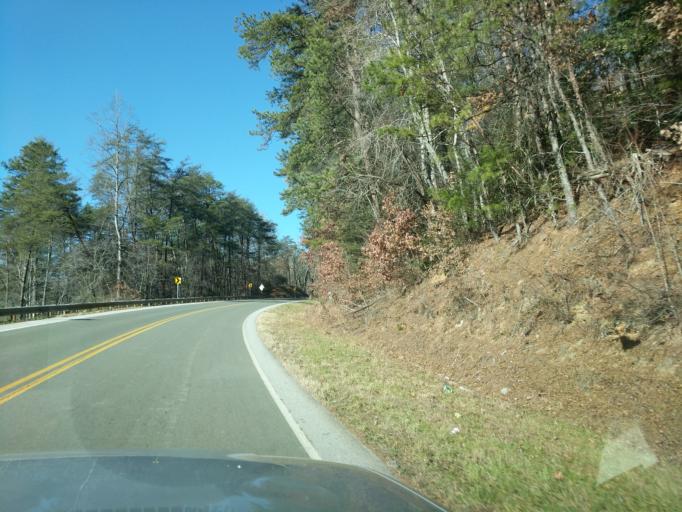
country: US
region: Georgia
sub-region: Rabun County
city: Clayton
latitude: 34.8484
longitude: -83.3601
